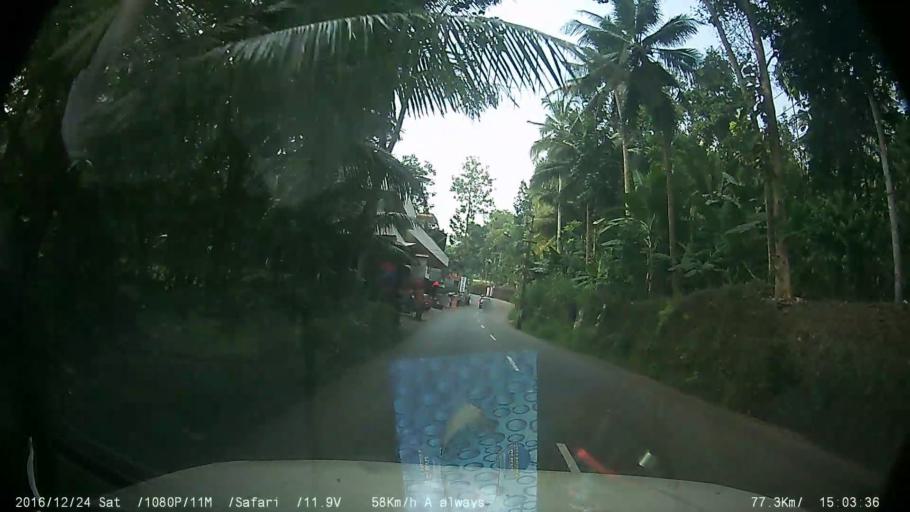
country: IN
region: Kerala
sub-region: Kottayam
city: Lalam
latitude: 9.7140
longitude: 76.6669
